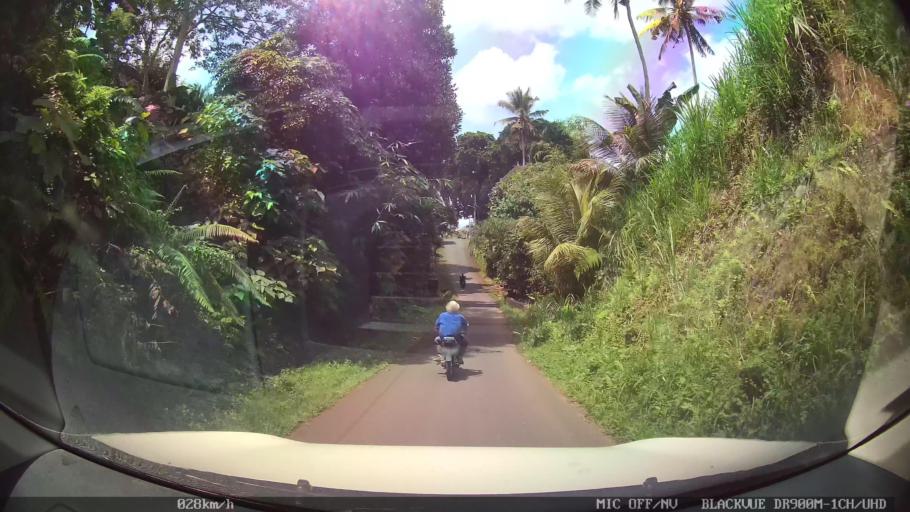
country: ID
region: Bali
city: Banjar Kelodan
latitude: -8.5182
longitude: 115.3740
